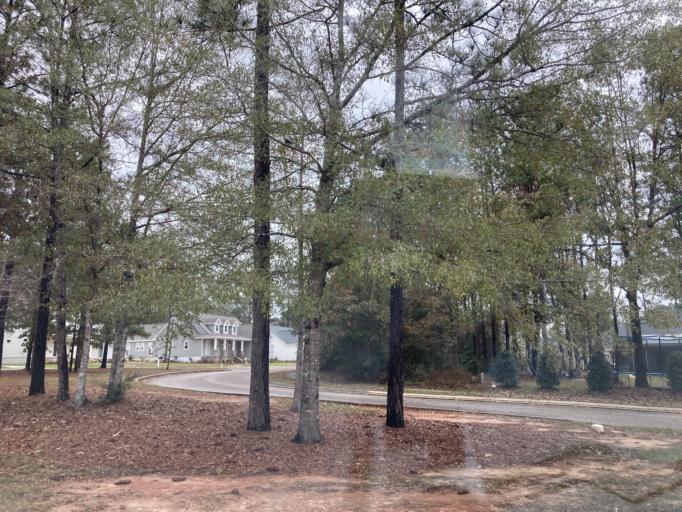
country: US
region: Mississippi
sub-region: Lamar County
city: West Hattiesburg
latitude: 31.2872
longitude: -89.4789
